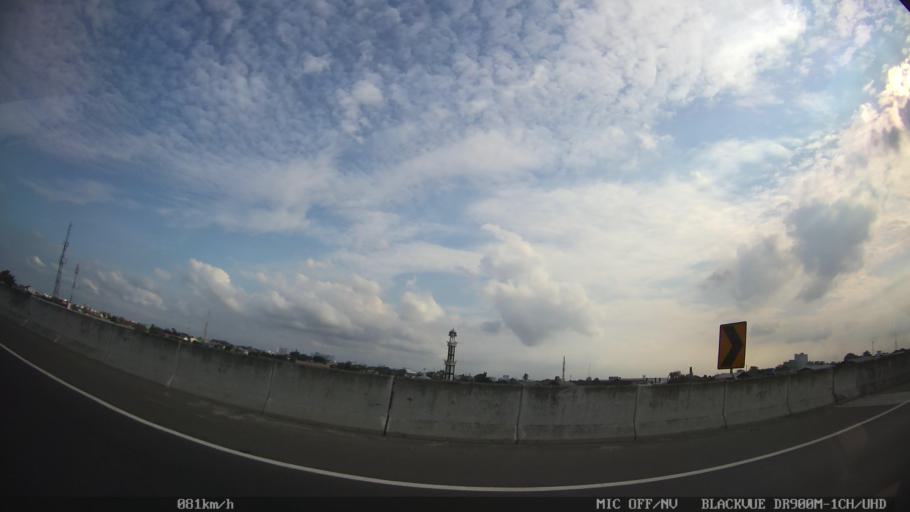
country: ID
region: North Sumatra
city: Medan
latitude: 3.6475
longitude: 98.6694
